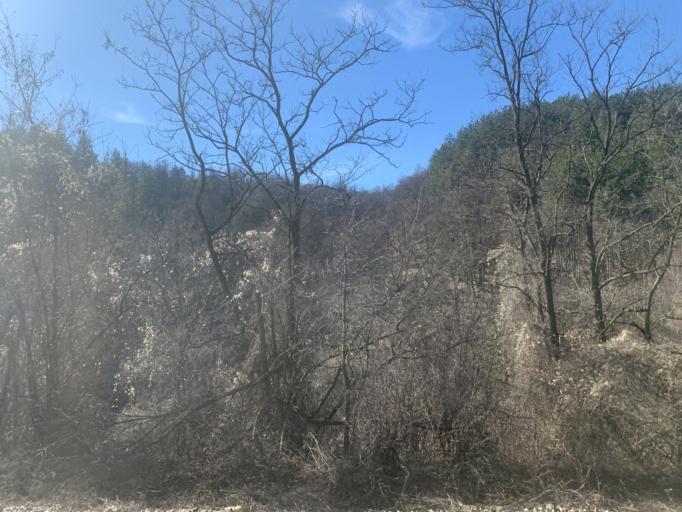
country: BG
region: Sofiya
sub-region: Obshtina Gorna Malina
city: Gorna Malina
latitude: 42.5689
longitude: 23.6733
